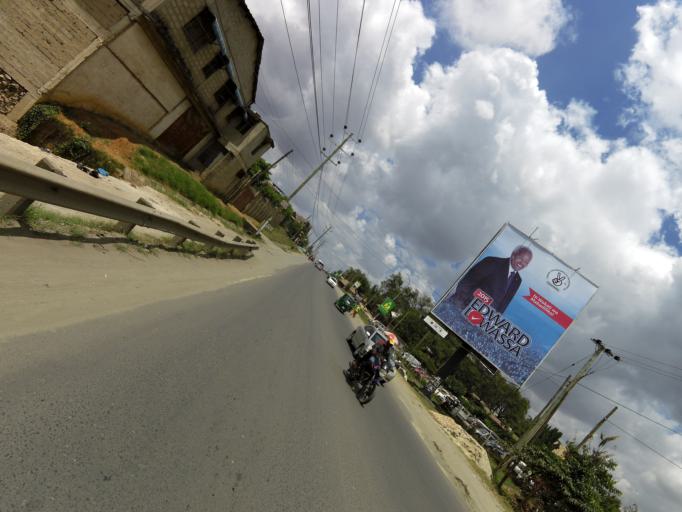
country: TZ
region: Dar es Salaam
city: Magomeni
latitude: -6.7915
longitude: 39.2202
